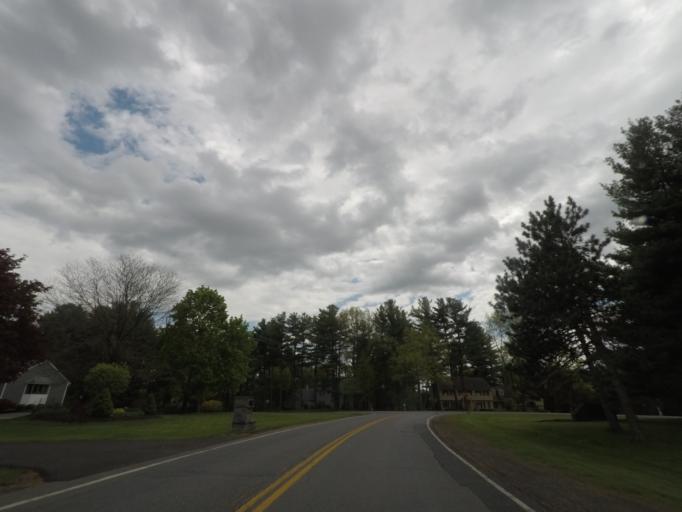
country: US
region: New York
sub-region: Albany County
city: Voorheesville
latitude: 42.6725
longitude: -73.9181
